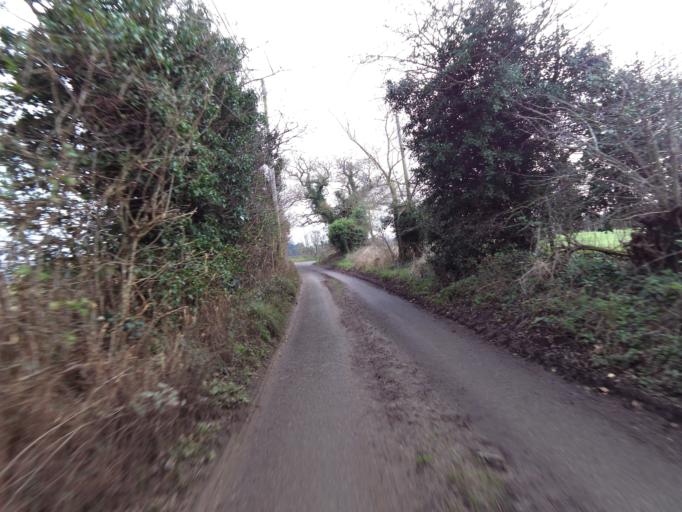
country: GB
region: England
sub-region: Suffolk
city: Woodbridge
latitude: 52.0588
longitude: 1.3172
